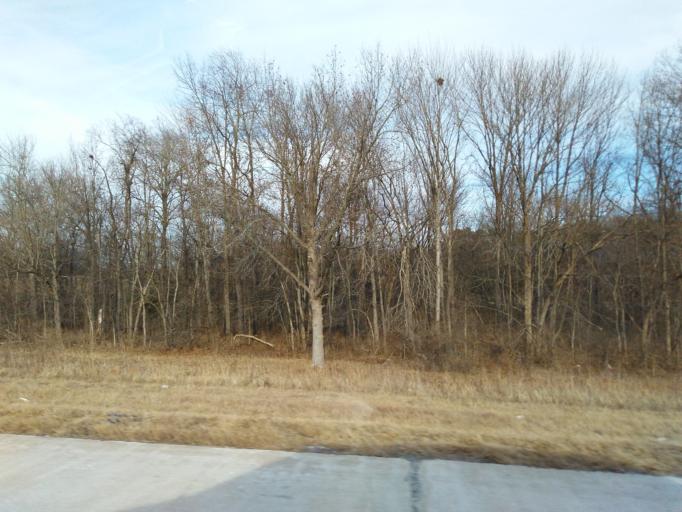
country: US
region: Illinois
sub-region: Jefferson County
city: Mount Vernon
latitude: 38.2780
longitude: -88.9363
